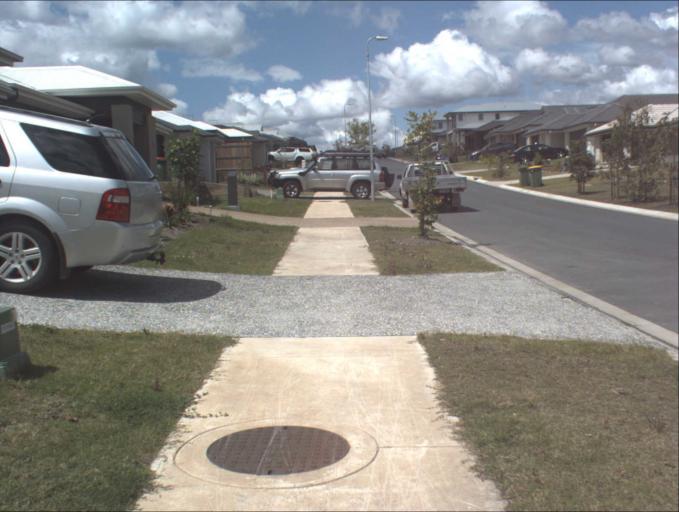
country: AU
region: Queensland
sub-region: Logan
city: Chambers Flat
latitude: -27.8054
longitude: 153.1118
